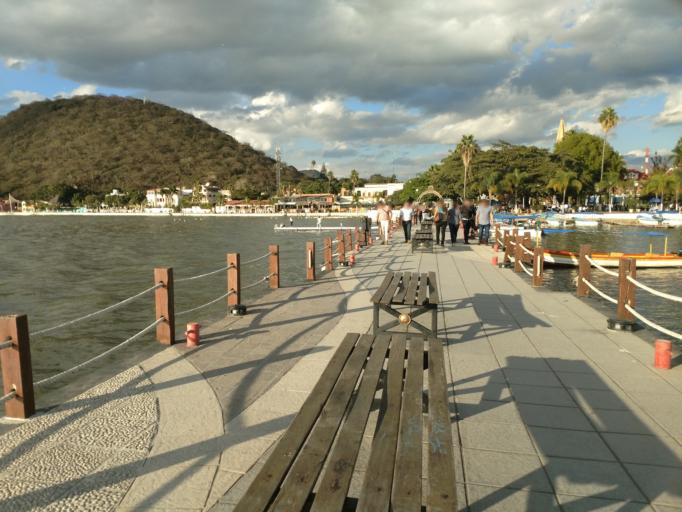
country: MX
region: Jalisco
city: Chapala
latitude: 20.2867
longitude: -103.1939
